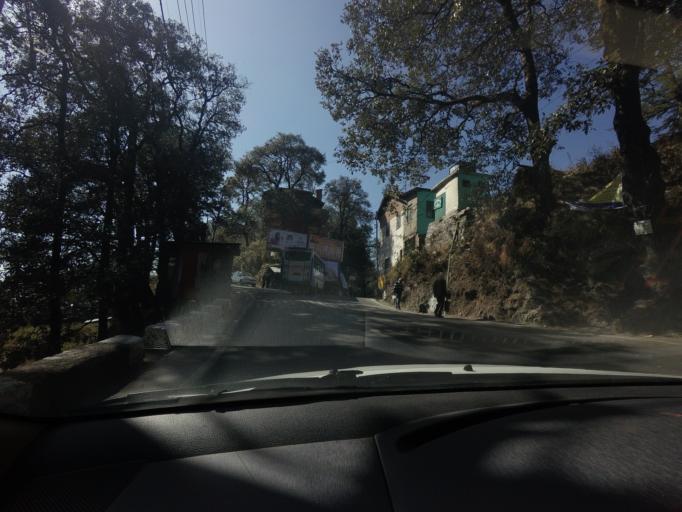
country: IN
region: Himachal Pradesh
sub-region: Shimla
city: Jutogh
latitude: 31.0997
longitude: 77.1391
